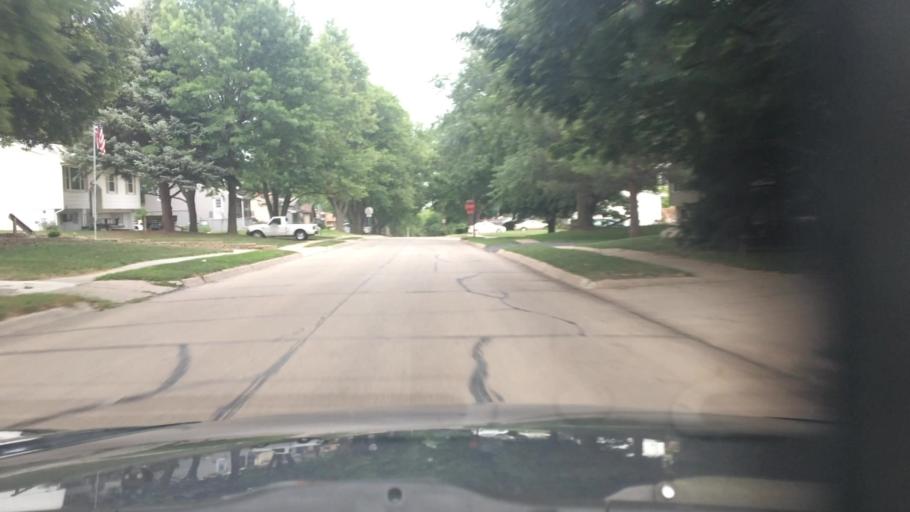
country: US
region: Nebraska
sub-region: Douglas County
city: Ralston
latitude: 41.1882
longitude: -96.0516
